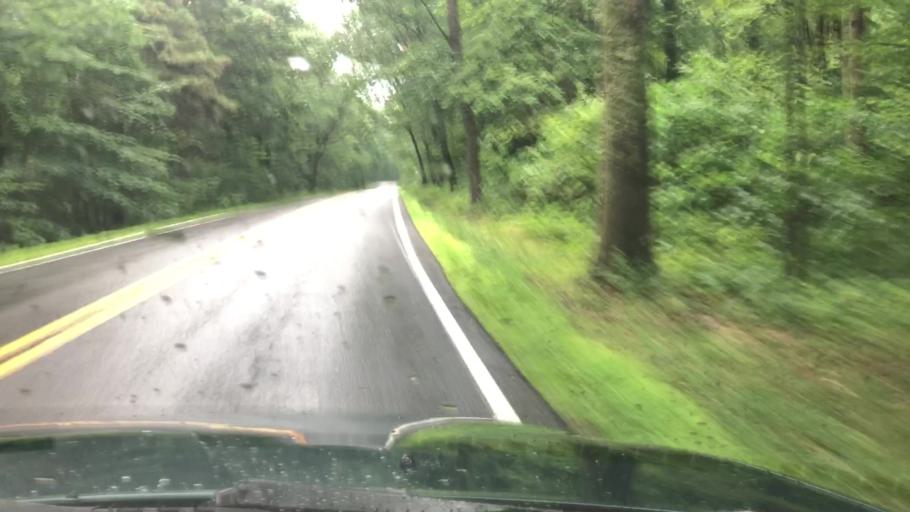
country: US
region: Pennsylvania
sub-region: Wayne County
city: Hawley
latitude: 41.3522
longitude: -75.2108
